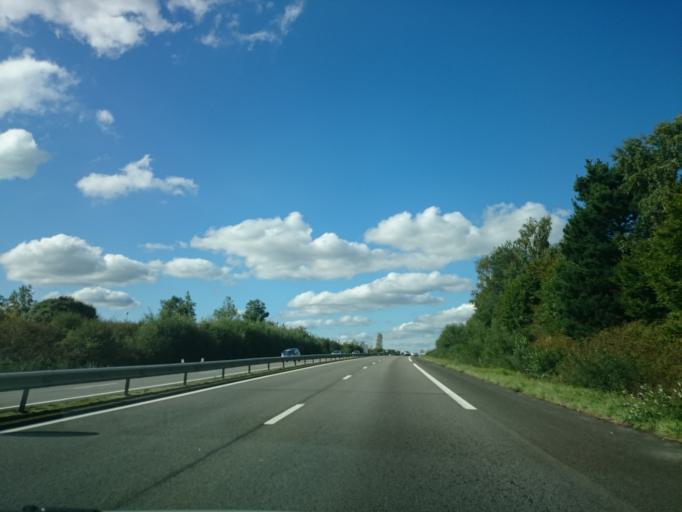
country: FR
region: Pays de la Loire
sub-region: Departement de la Loire-Atlantique
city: Treillieres
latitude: 47.3360
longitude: -1.6534
